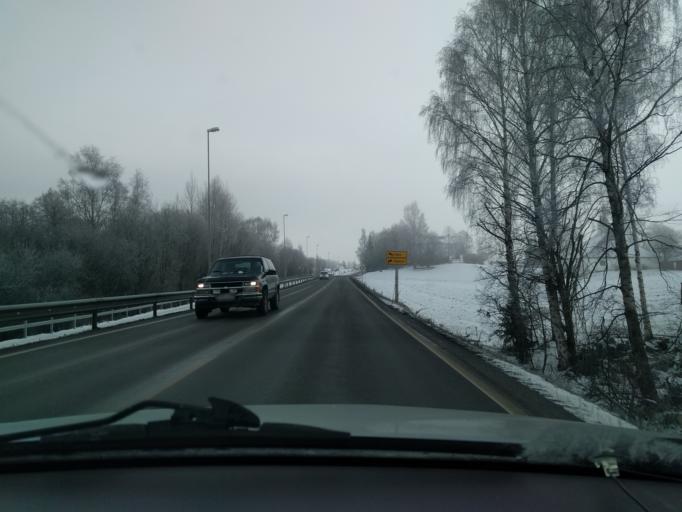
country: NO
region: Hedmark
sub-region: Hamar
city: Hamar
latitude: 60.8038
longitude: 11.1426
